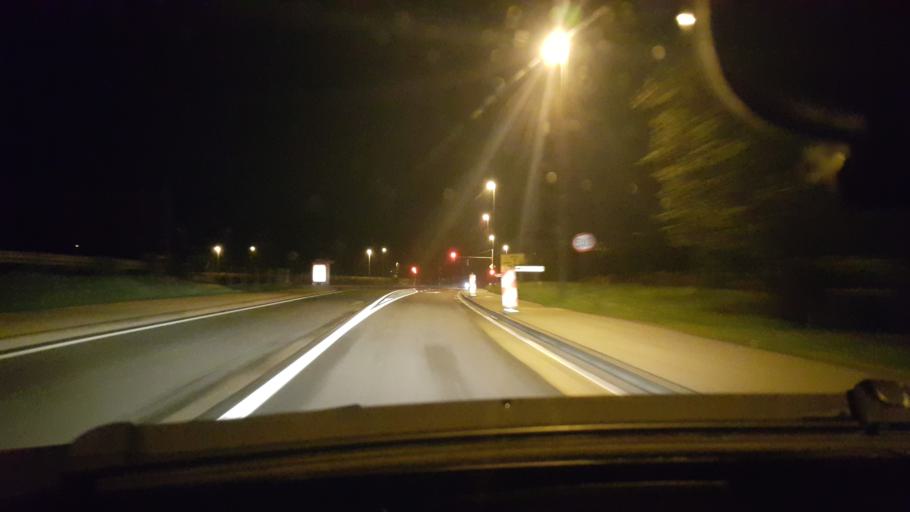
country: SI
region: Maribor
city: Kamnica
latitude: 46.5709
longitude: 15.6116
